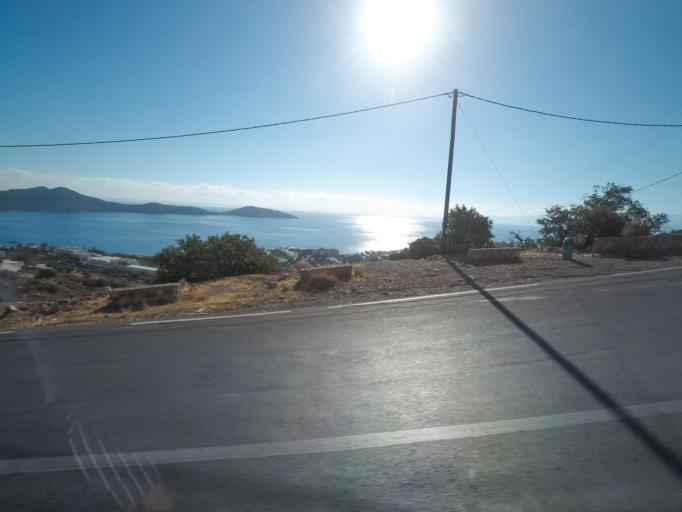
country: GR
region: Crete
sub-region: Nomos Lasithiou
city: Skhisma
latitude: 35.2385
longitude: 25.7269
